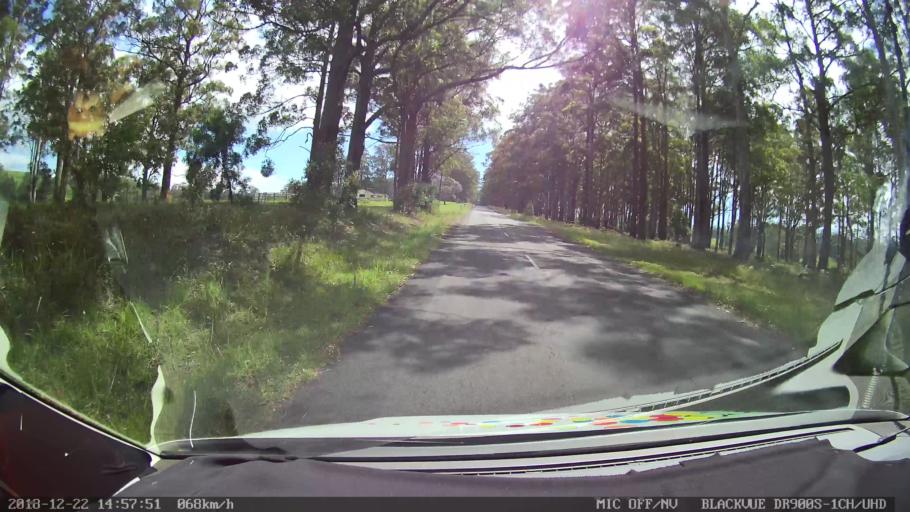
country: AU
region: New South Wales
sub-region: Bellingen
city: Dorrigo
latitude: -30.2367
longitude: 152.4967
